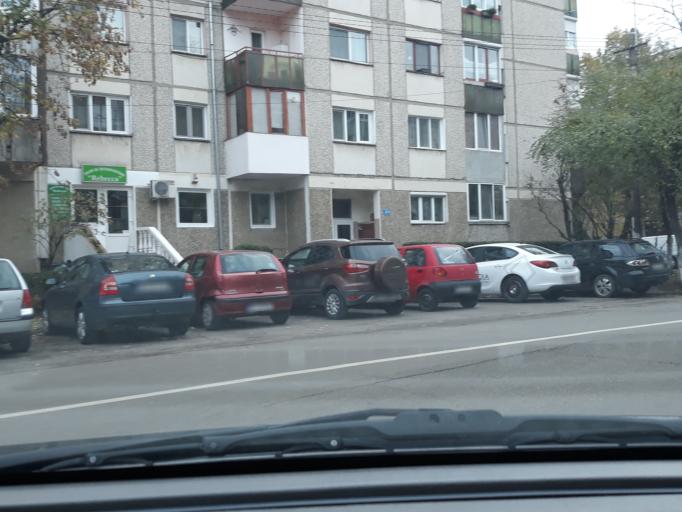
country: RO
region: Bihor
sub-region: Comuna Biharea
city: Oradea
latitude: 47.0675
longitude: 21.9229
